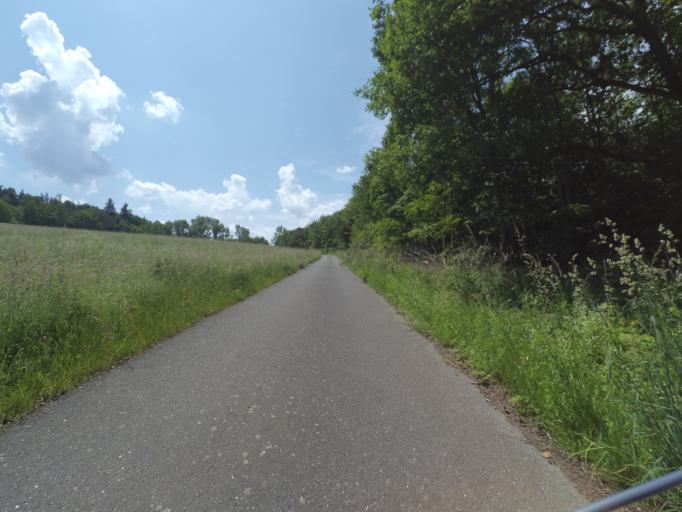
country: DE
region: Rheinland-Pfalz
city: Mermuth
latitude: 50.1643
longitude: 7.4739
